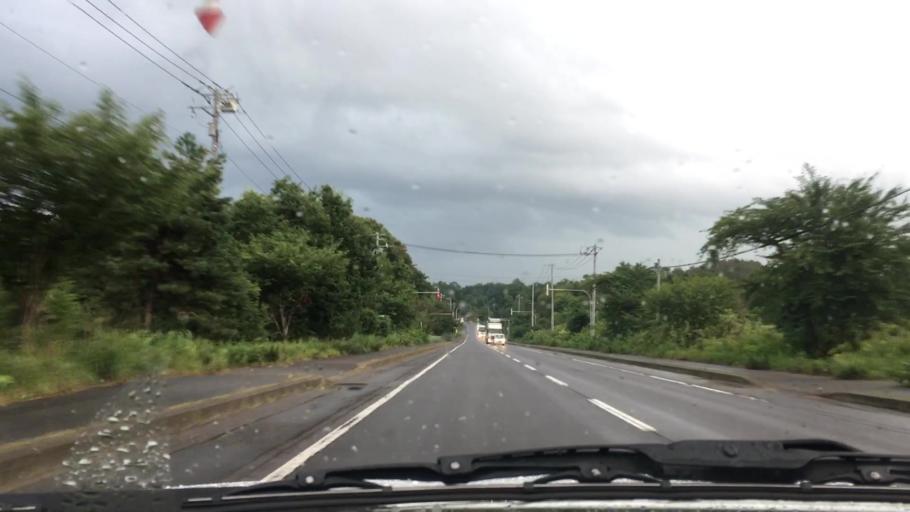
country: JP
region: Hokkaido
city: Nanae
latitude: 42.0872
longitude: 140.5832
